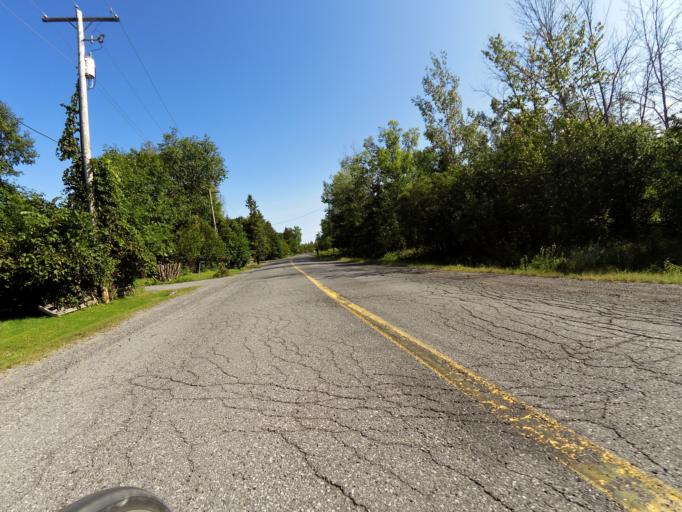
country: CA
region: Ontario
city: Bells Corners
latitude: 45.4587
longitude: -75.9684
